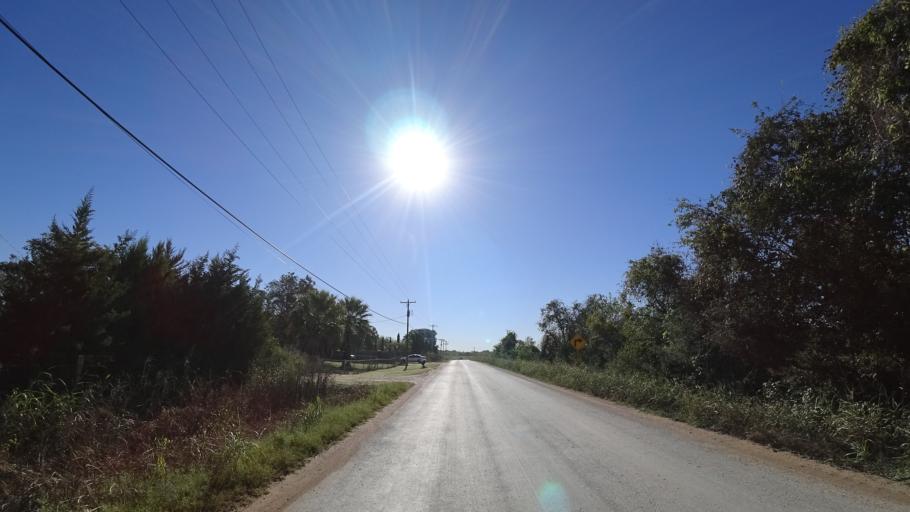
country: US
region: Texas
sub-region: Travis County
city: Hornsby Bend
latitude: 30.2448
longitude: -97.6535
